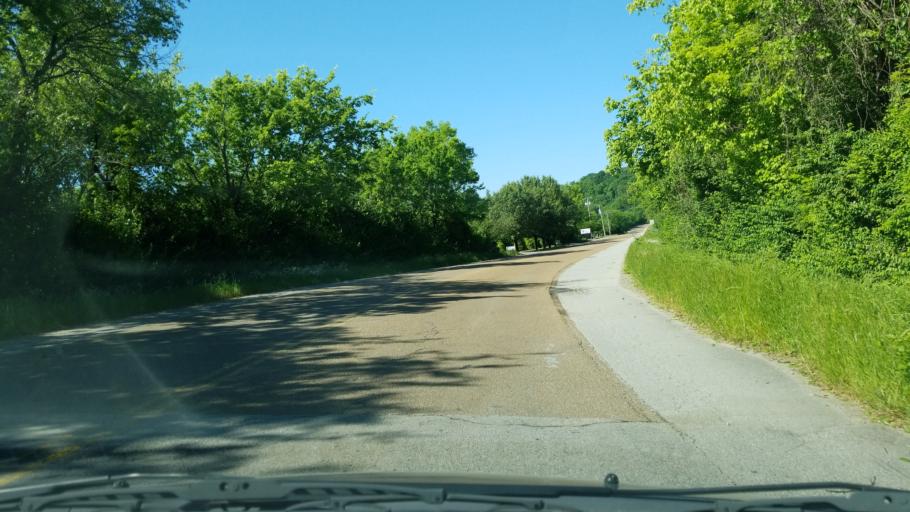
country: US
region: Tennessee
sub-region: Hamilton County
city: Chattanooga
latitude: 35.0565
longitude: -85.3247
